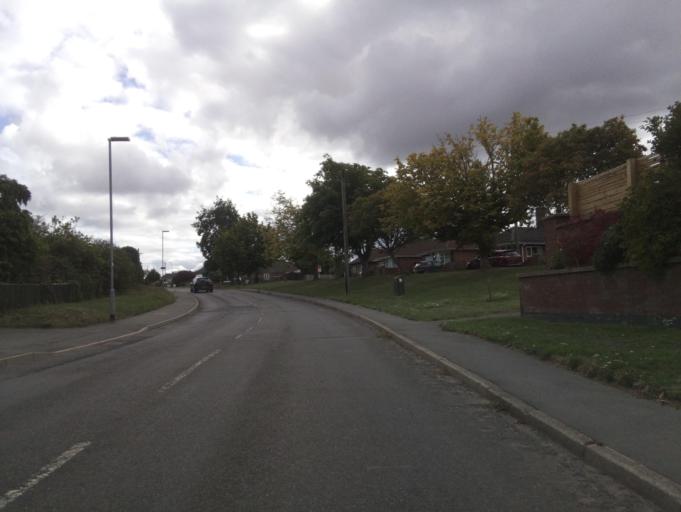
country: GB
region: England
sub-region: Nottinghamshire
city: East Leake
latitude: 52.8295
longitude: -1.1735
